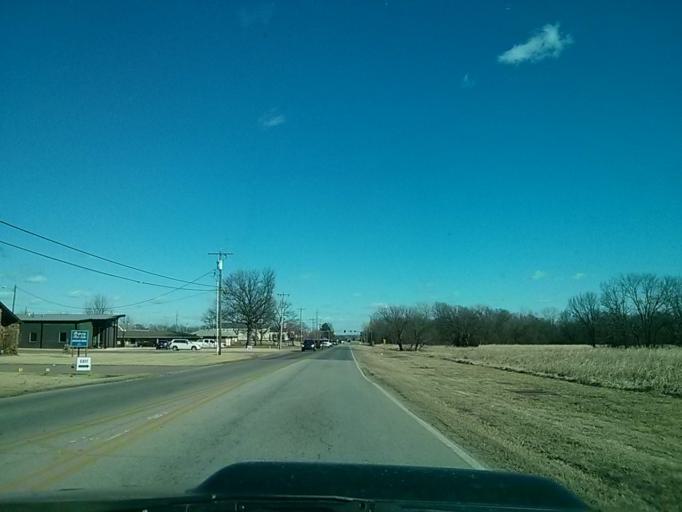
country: US
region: Oklahoma
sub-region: Tulsa County
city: Jenks
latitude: 36.0247
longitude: -96.0076
